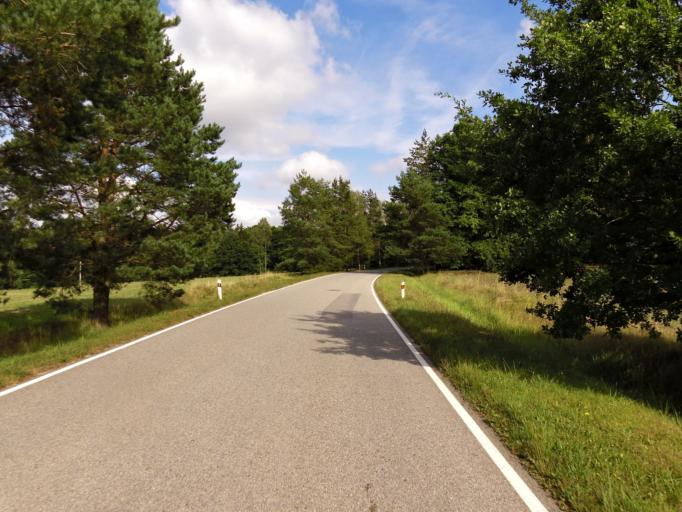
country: CZ
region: Jihocesky
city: Suchdol nad Luznici
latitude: 48.8886
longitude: 14.8046
